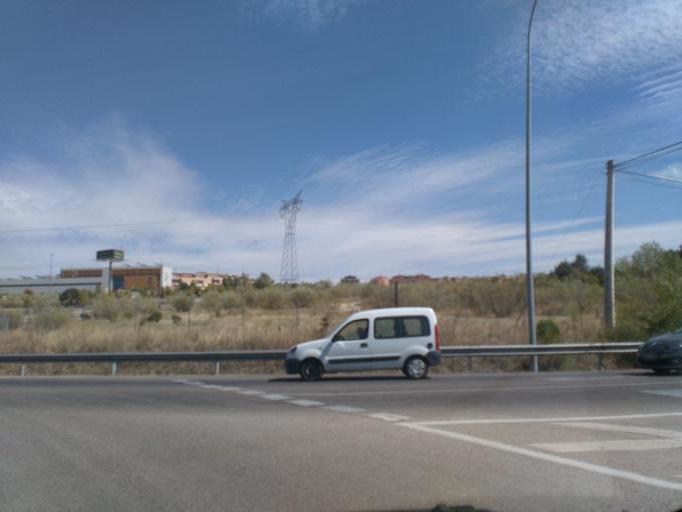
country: ES
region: Madrid
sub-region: Provincia de Madrid
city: Villanueva del Pardillo
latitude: 40.5189
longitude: -3.9375
